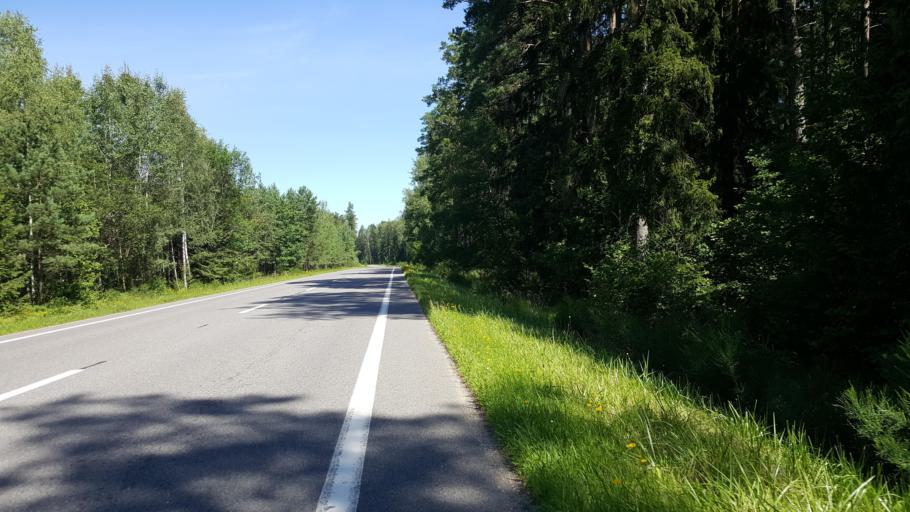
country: BY
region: Brest
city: Pruzhany
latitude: 52.5118
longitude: 24.1791
